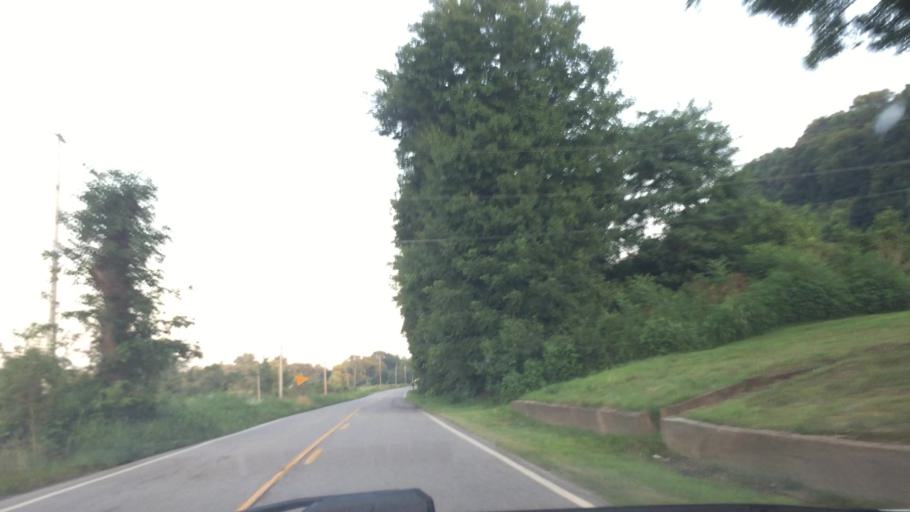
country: US
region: Kentucky
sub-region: Carroll County
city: Carrollton
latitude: 38.6728
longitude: -85.1940
